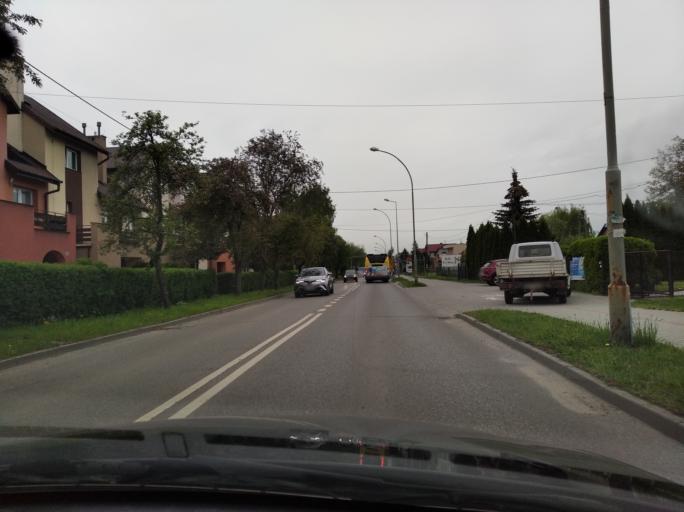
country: PL
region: Lesser Poland Voivodeship
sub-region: Powiat tarnowski
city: Tarnow
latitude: 50.0224
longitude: 20.9809
